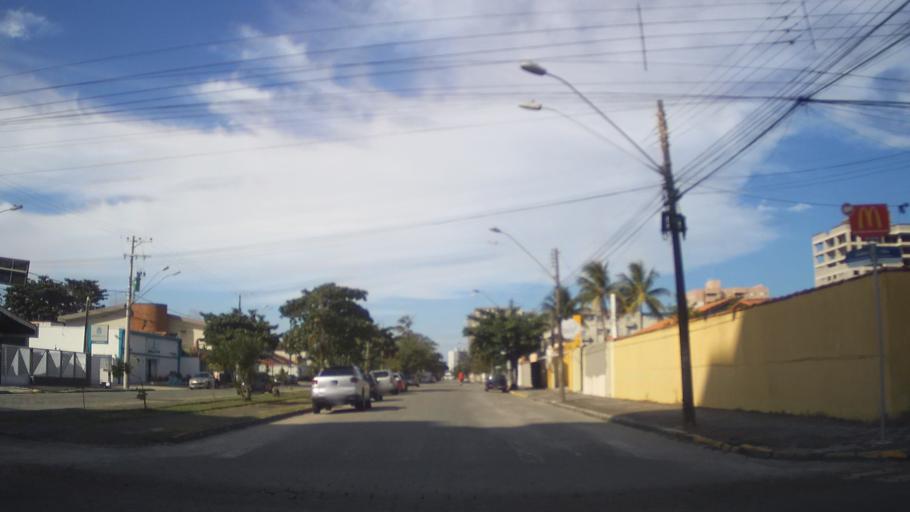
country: BR
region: Sao Paulo
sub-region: Itanhaem
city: Itanhaem
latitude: -24.1832
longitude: -46.7846
